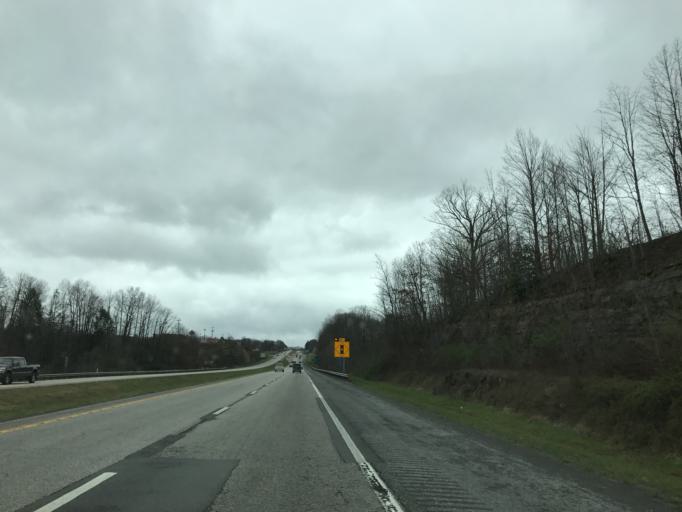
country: US
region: West Virginia
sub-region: Fayette County
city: Fayetteville
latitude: 38.0384
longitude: -81.1228
